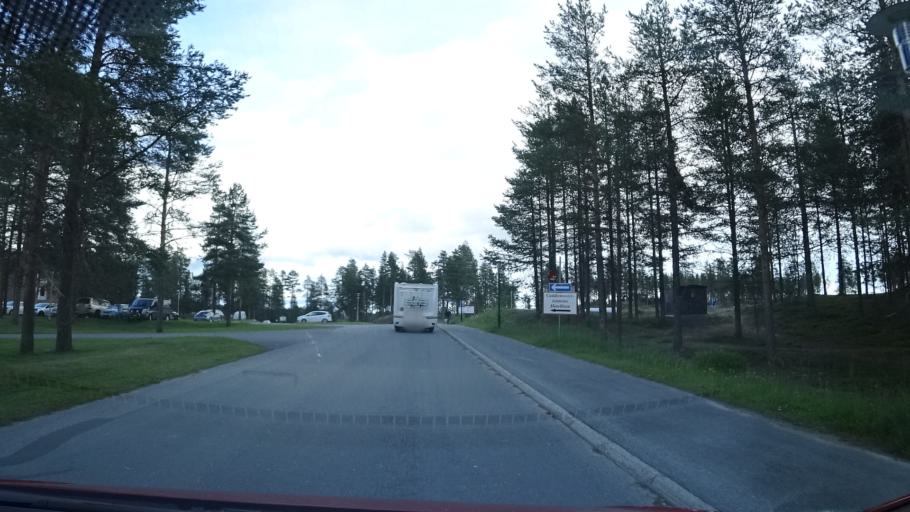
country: FI
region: Northern Ostrobothnia
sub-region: Koillismaa
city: Kuusamo
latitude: 66.0009
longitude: 29.1667
